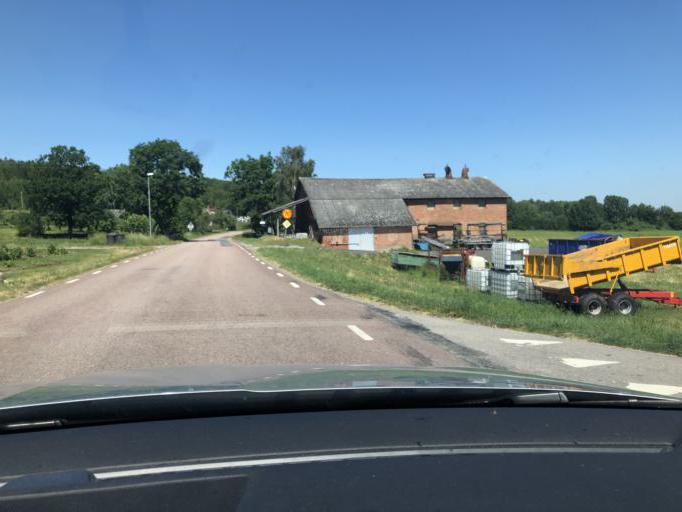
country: SE
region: Blekinge
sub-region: Olofstroms Kommun
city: Jamshog
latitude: 56.1609
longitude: 14.5994
